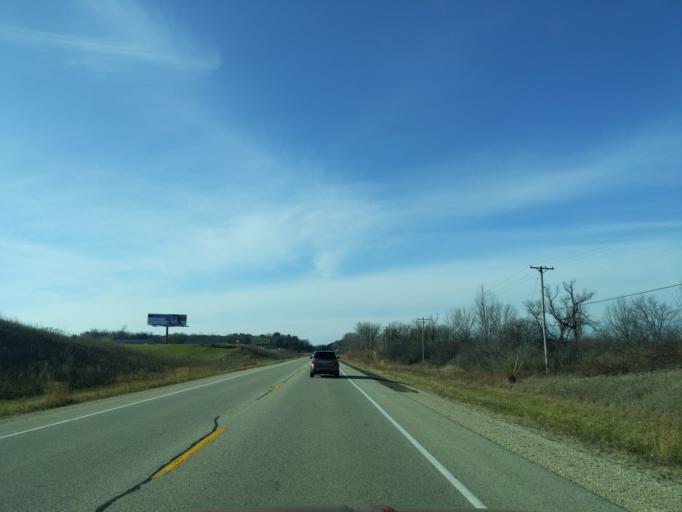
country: US
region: Wisconsin
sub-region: Rock County
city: Milton
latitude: 42.8258
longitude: -88.9914
